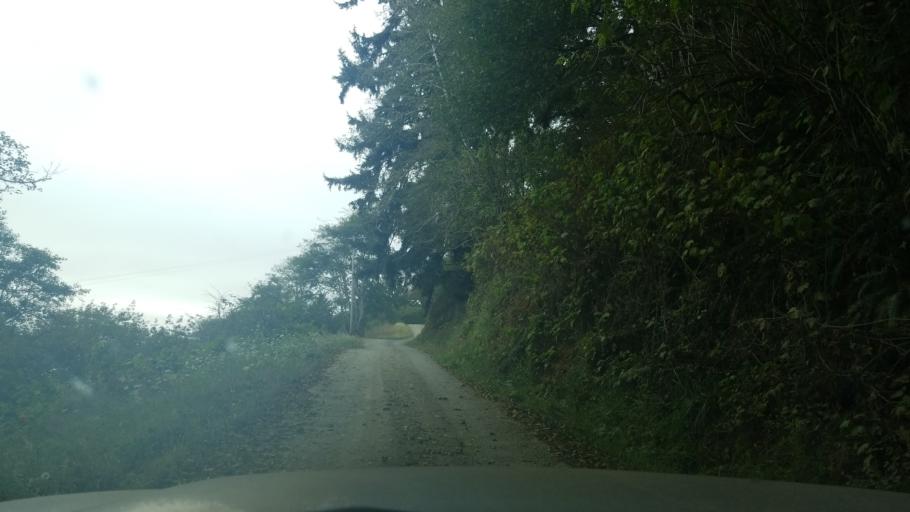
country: US
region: California
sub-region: Del Norte County
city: Bertsch-Oceanview
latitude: 41.5228
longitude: -124.0782
